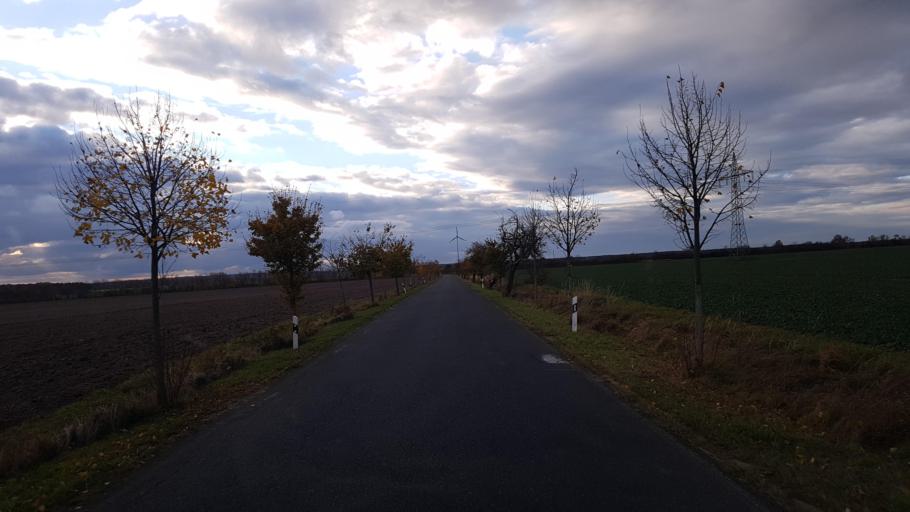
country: DE
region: Saxony-Anhalt
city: Zahna
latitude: 51.9458
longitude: 12.8219
